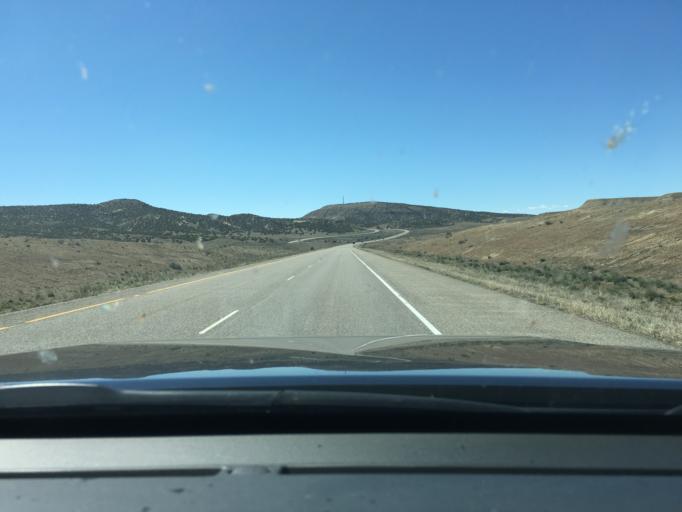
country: US
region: Colorado
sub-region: Mesa County
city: Loma
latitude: 39.2254
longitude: -108.9355
